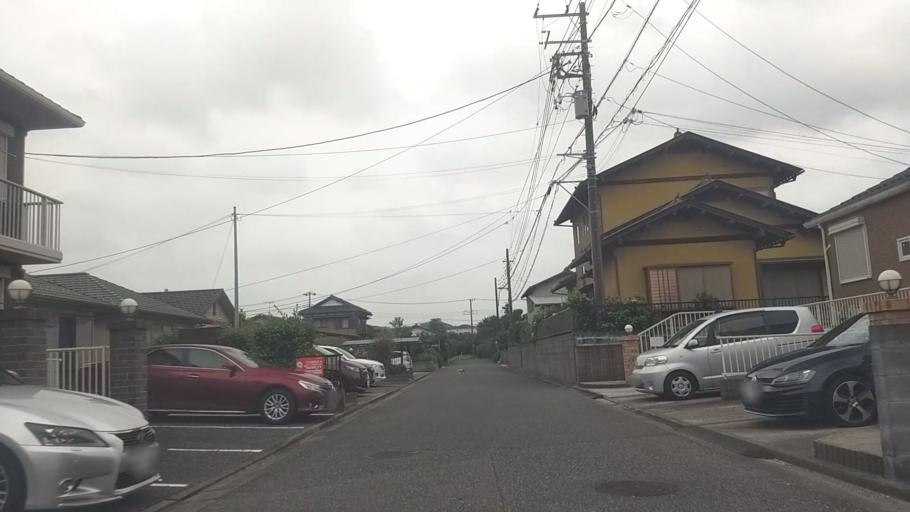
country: JP
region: Chiba
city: Kisarazu
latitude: 35.3861
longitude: 139.9665
